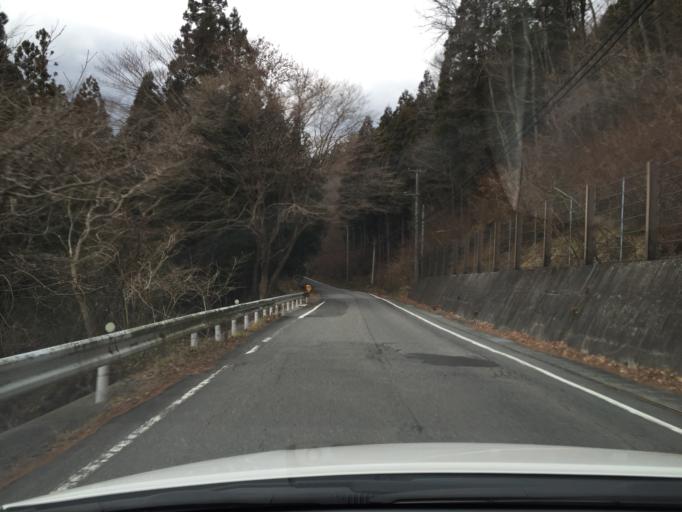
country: JP
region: Fukushima
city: Iwaki
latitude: 37.1209
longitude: 140.7764
